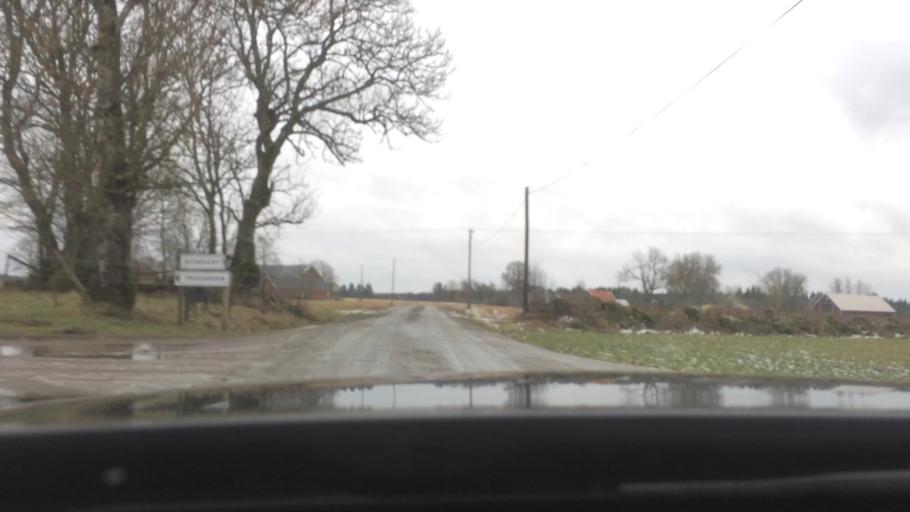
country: SE
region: Vaestra Goetaland
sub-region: Falkopings Kommun
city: Floby
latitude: 57.9941
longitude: 13.3982
